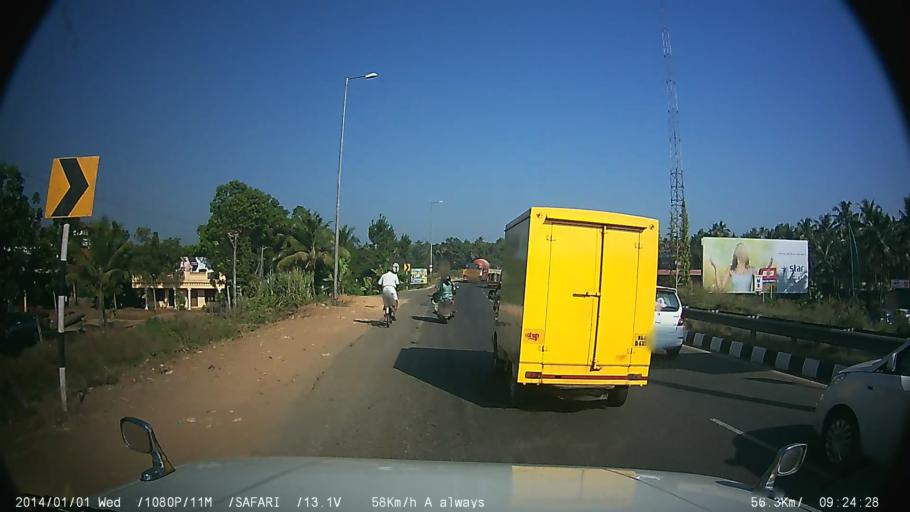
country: IN
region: Kerala
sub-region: Thrissur District
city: Kizhake Chalakudi
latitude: 10.2901
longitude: 76.3362
